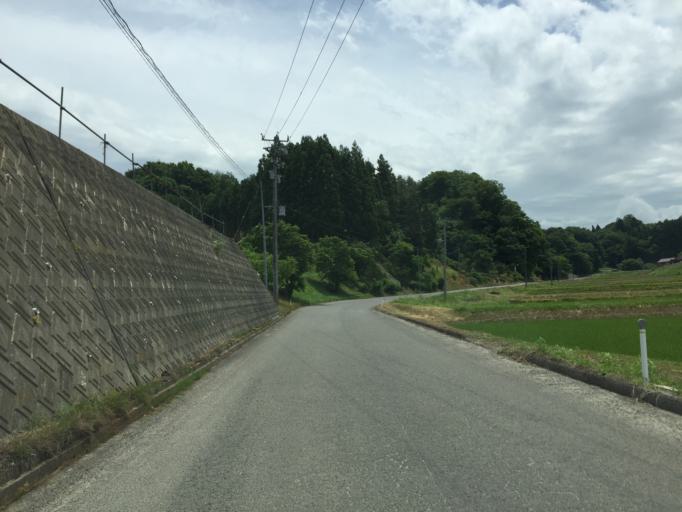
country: JP
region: Fukushima
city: Miharu
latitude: 37.4117
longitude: 140.5232
